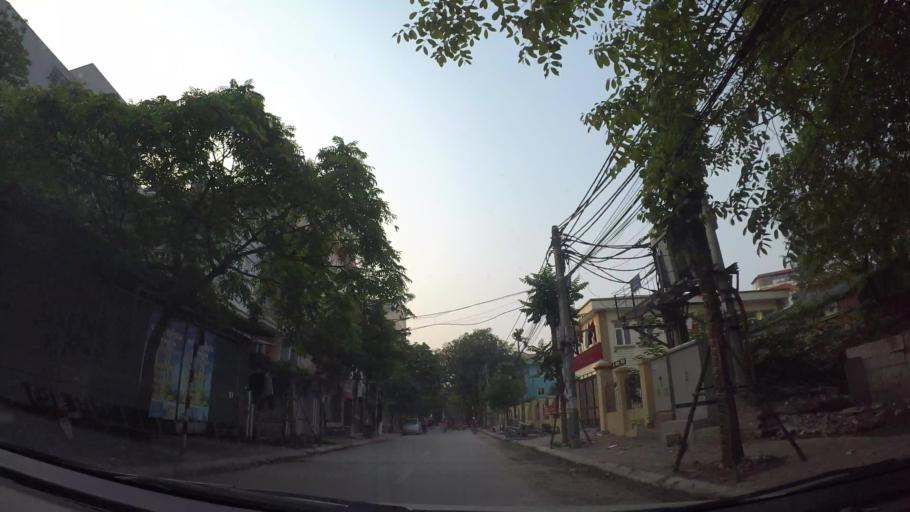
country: VN
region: Ha Noi
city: Tay Ho
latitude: 21.0676
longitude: 105.7891
